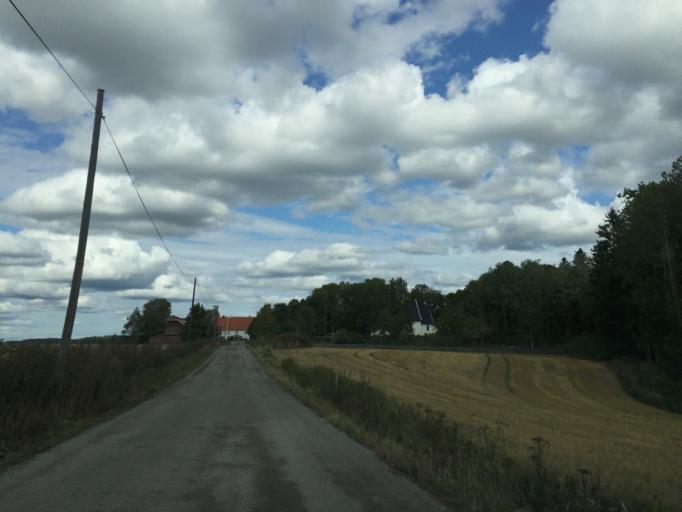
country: NO
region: Ostfold
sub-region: Hobol
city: Elvestad
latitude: 59.5988
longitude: 10.9217
